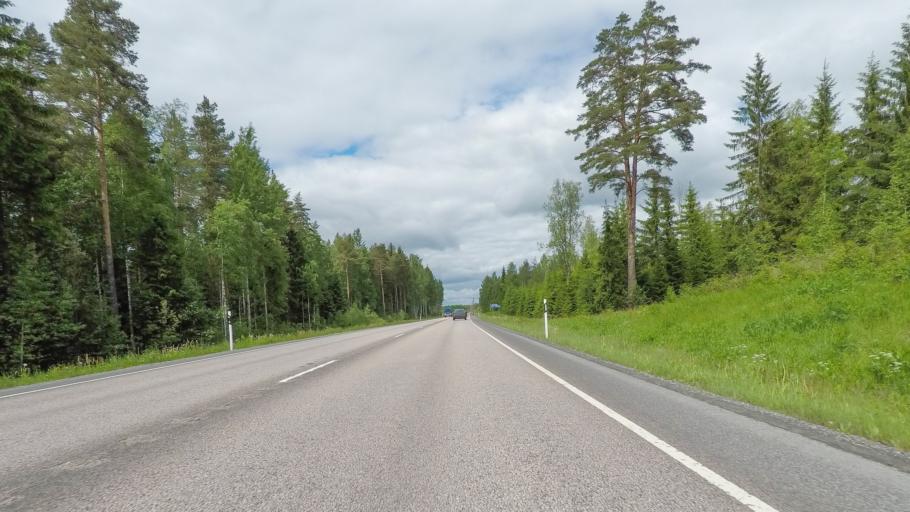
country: FI
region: Paijanne Tavastia
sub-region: Lahti
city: Hartola
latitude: 61.5952
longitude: 26.0081
